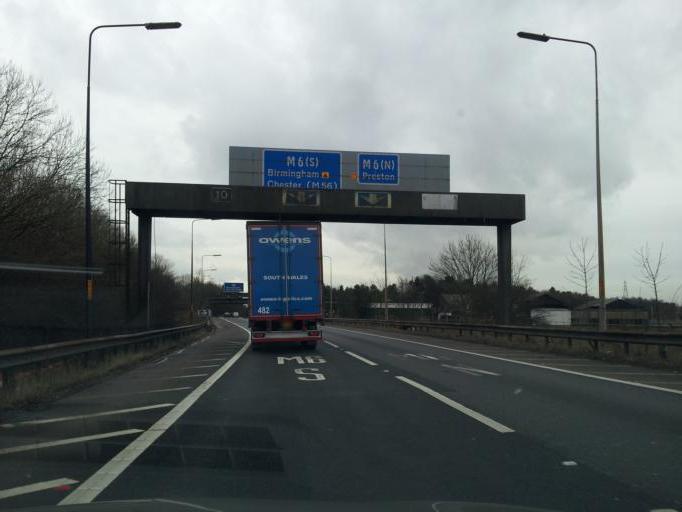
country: GB
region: England
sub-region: Warrington
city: Croft
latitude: 53.4280
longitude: -2.5437
